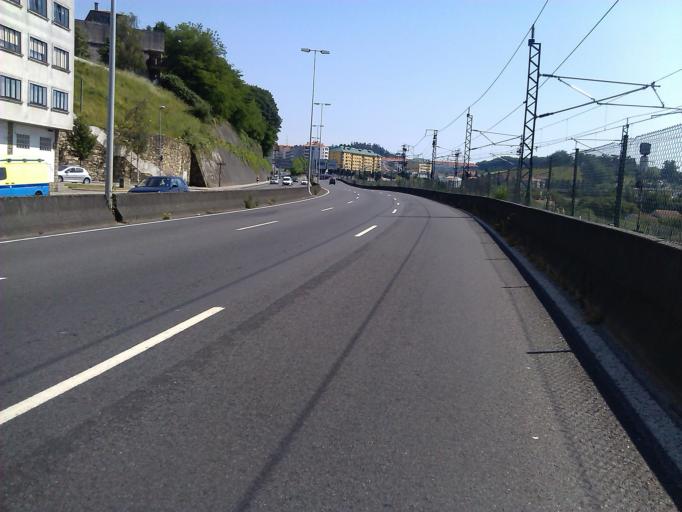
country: ES
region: Galicia
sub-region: Provincia da Coruna
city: Santiago de Compostela
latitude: 42.8742
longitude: -8.5365
